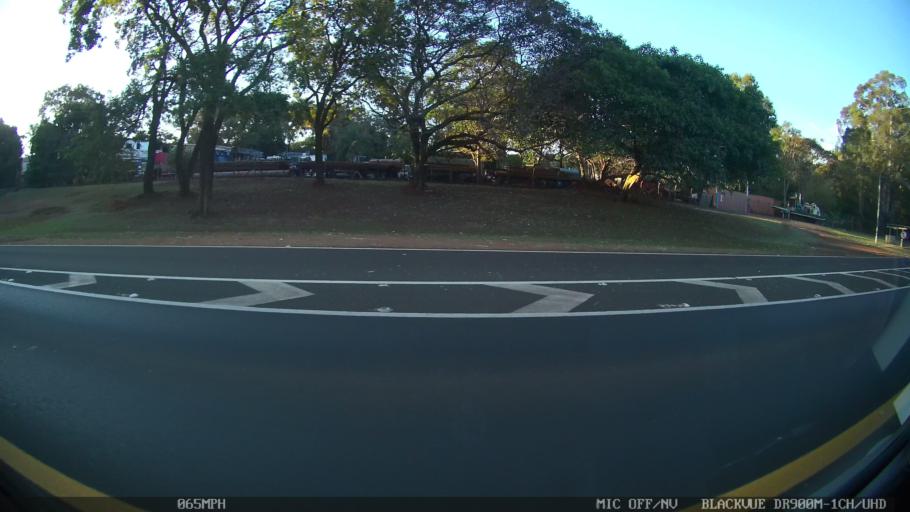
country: BR
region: Sao Paulo
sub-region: Araraquara
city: Araraquara
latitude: -21.8170
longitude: -48.1979
